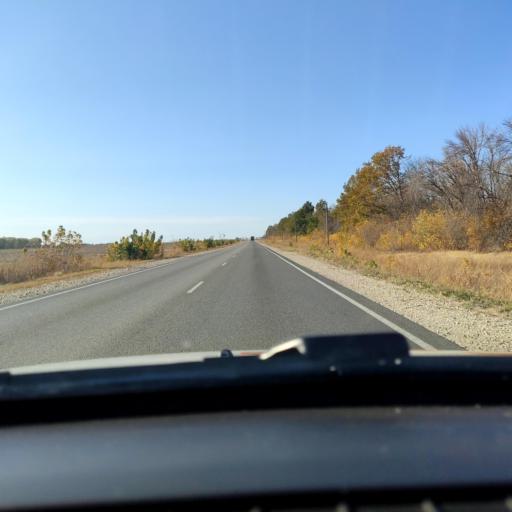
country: RU
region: Voronezj
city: Semiluki
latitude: 51.7306
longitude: 38.9728
